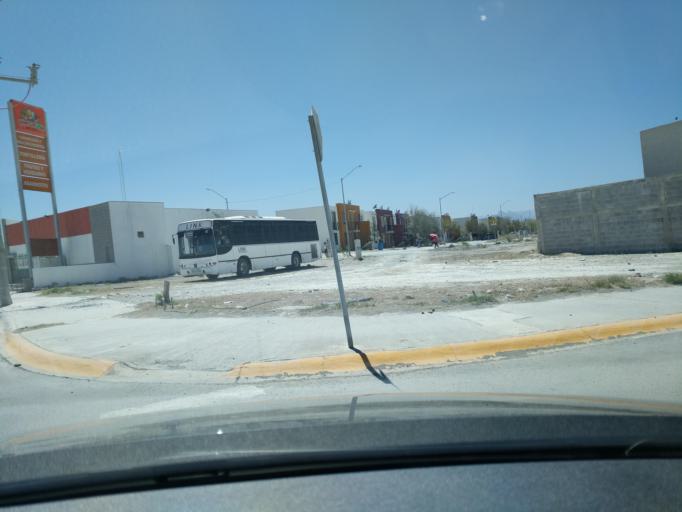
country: MX
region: Nuevo Leon
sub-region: Apodaca
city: Artemio Trevino
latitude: 25.8409
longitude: -100.1432
